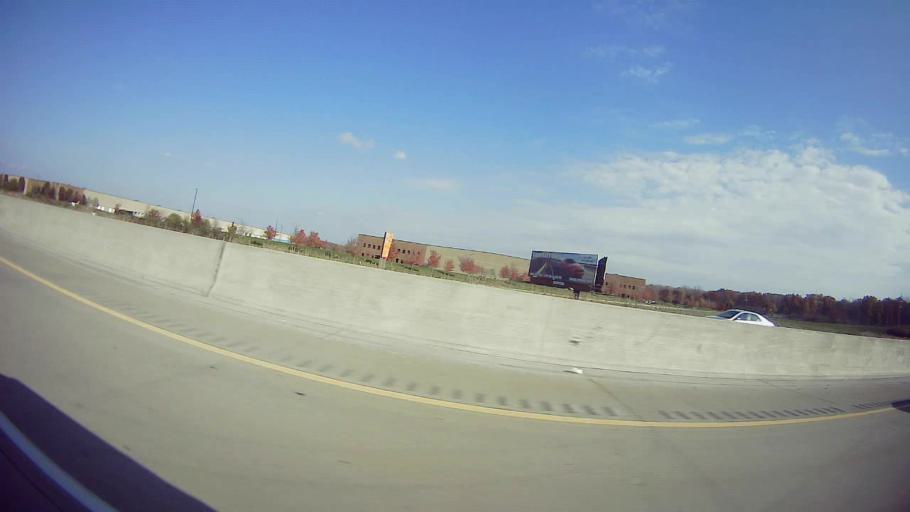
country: US
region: Michigan
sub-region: Wayne County
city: Woodhaven
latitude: 42.1565
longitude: -83.2426
